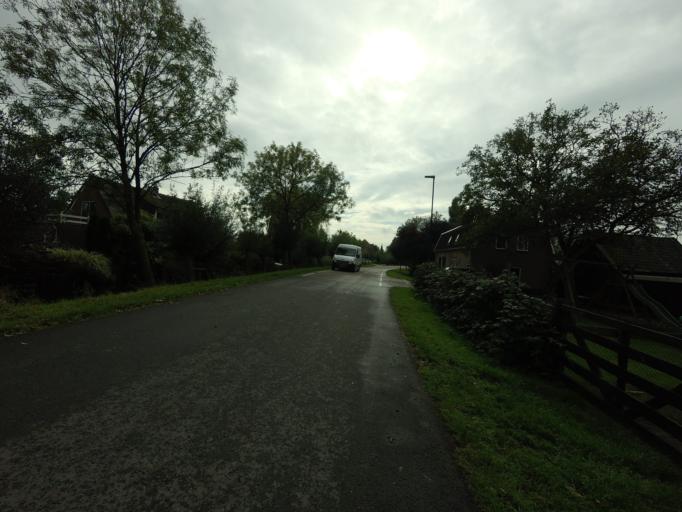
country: NL
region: Utrecht
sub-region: Gemeente Lopik
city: Lopik
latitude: 51.9098
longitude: 4.9562
